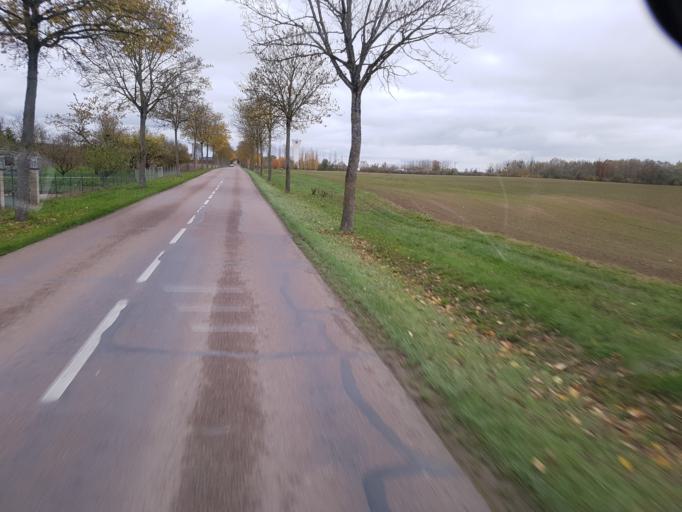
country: FR
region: Champagne-Ardenne
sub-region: Departement de l'Aube
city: Mery-sur-Seine
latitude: 48.5158
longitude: 3.8787
